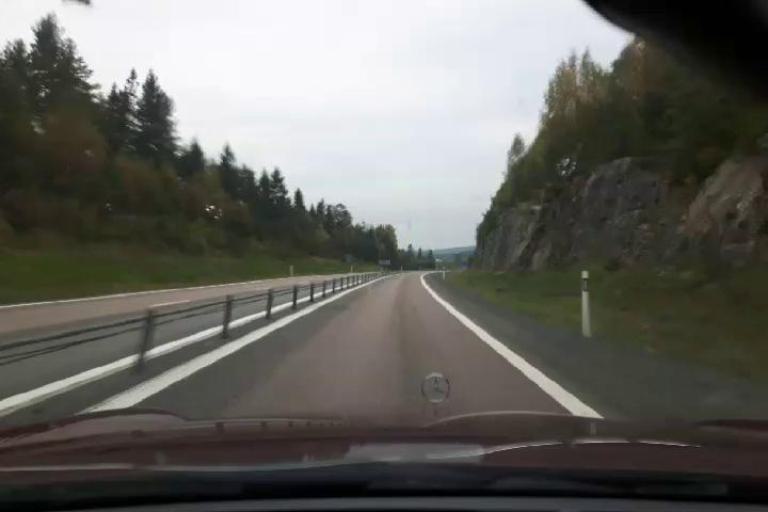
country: SE
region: Vaesternorrland
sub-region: Haernoesands Kommun
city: Haernoesand
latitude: 62.8597
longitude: 18.0257
